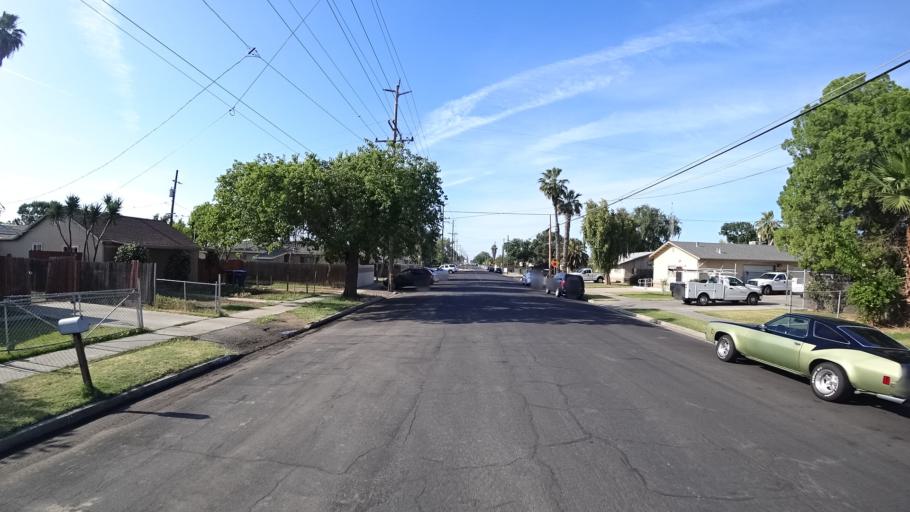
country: US
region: California
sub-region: Kings County
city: Hanford
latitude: 36.3181
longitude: -119.6460
